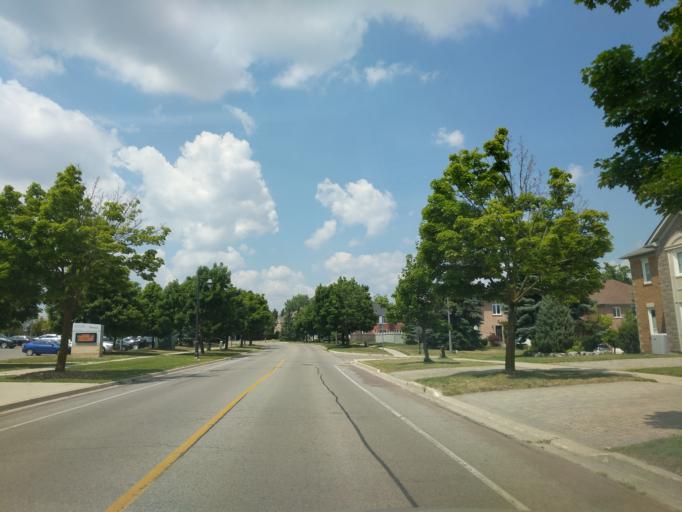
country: CA
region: Ontario
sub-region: York
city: Richmond Hill
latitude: 43.8693
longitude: -79.4009
